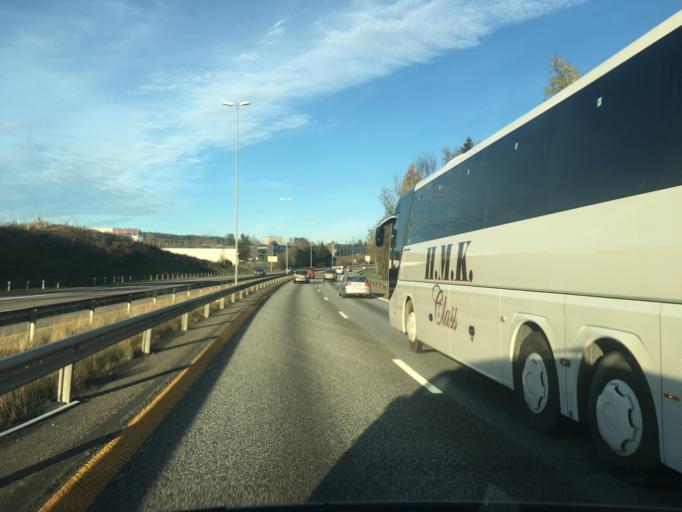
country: NO
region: Akershus
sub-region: Skedsmo
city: Leirsund
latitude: 60.0048
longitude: 11.0470
